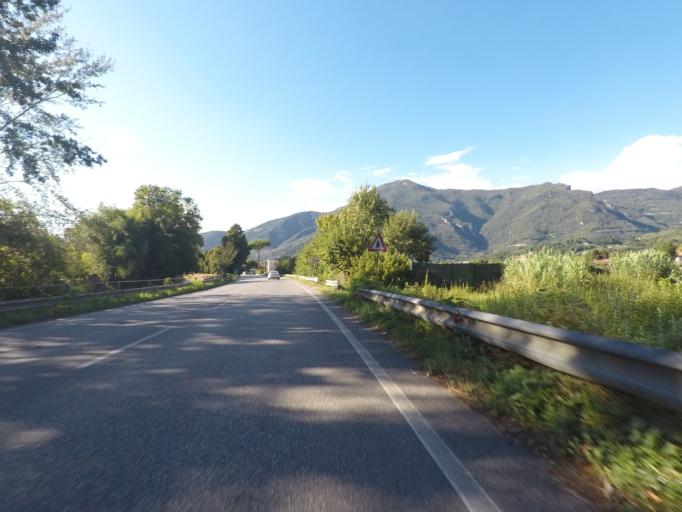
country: IT
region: Tuscany
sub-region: Provincia di Lucca
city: Corsanico-Bargecchia
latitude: 43.9319
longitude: 10.3107
